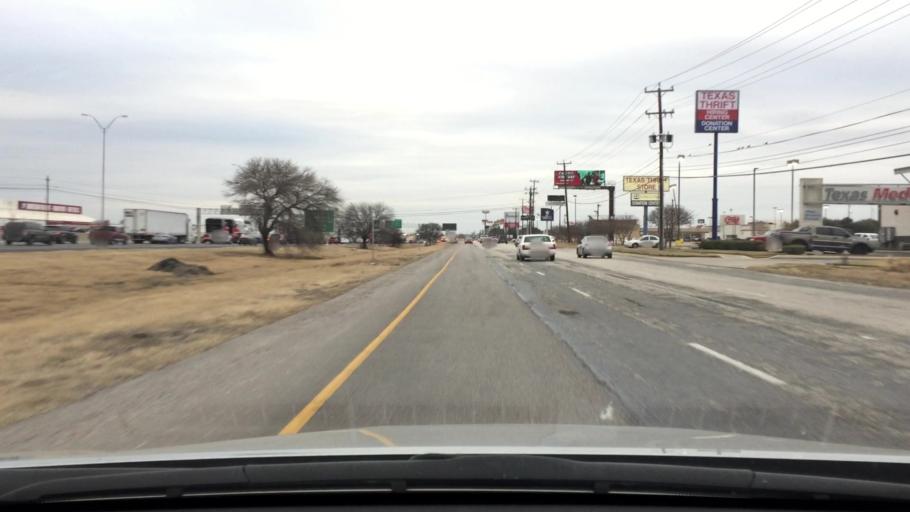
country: US
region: Texas
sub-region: Bexar County
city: Windcrest
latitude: 29.5013
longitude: -98.3991
